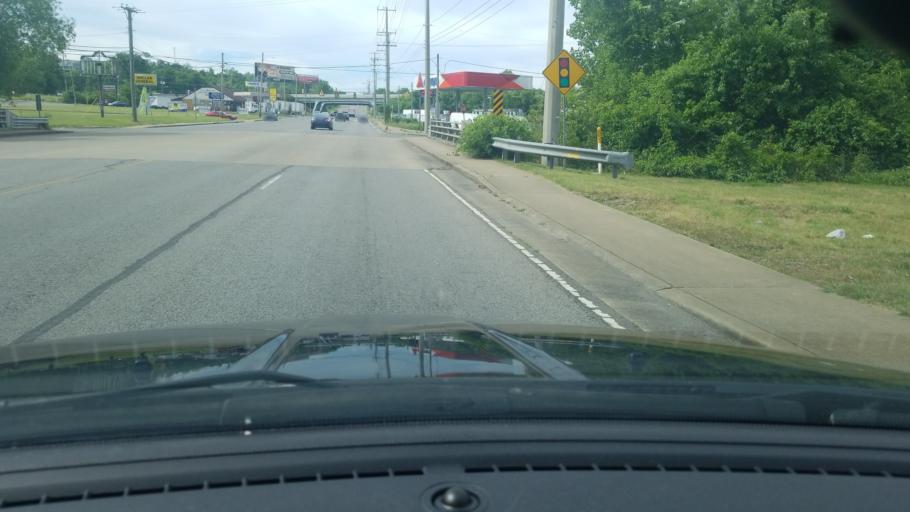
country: US
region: Tennessee
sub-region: Davidson County
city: Nashville
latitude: 36.2332
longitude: -86.7815
